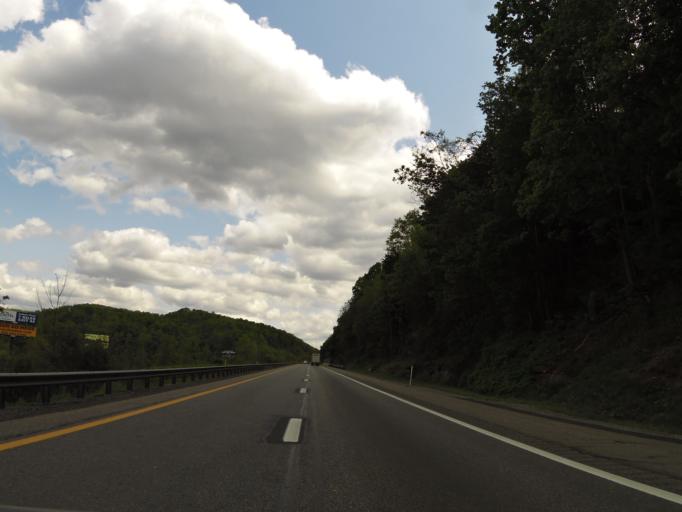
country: US
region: West Virginia
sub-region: Raleigh County
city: Bradley
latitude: 37.8774
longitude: -81.2664
